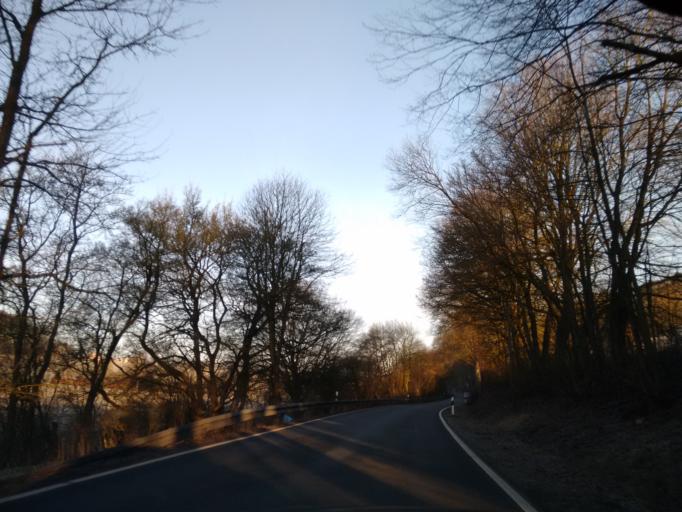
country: DE
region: North Rhine-Westphalia
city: Lichtenau
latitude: 51.6906
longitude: 8.8628
